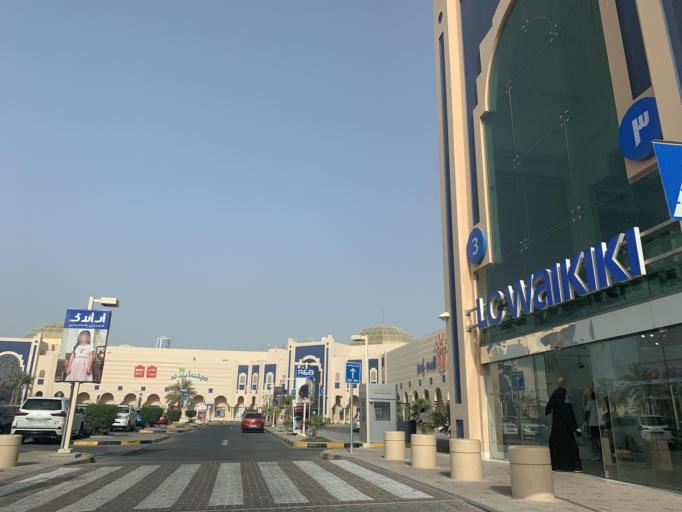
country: BH
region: Manama
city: Jidd Hafs
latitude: 26.2326
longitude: 50.5361
